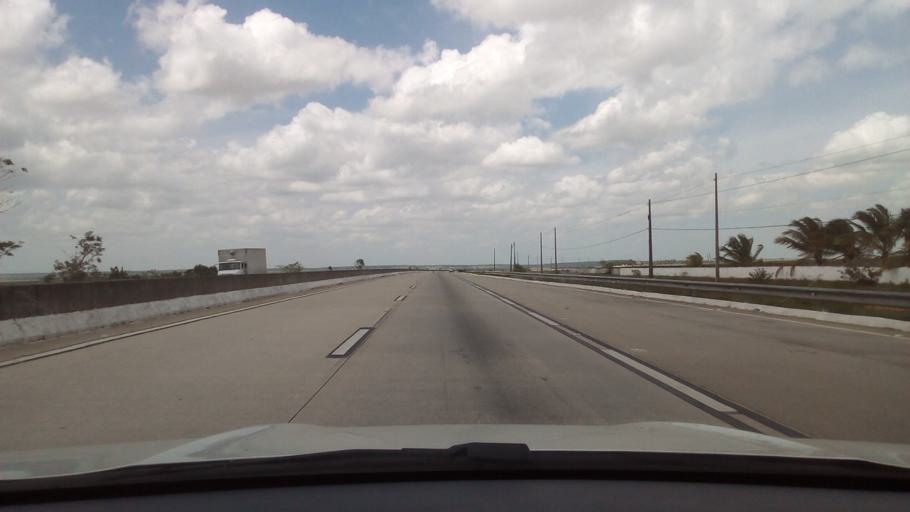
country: BR
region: Paraiba
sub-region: Mamanguape
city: Mamanguape
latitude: -6.8081
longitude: -35.1400
